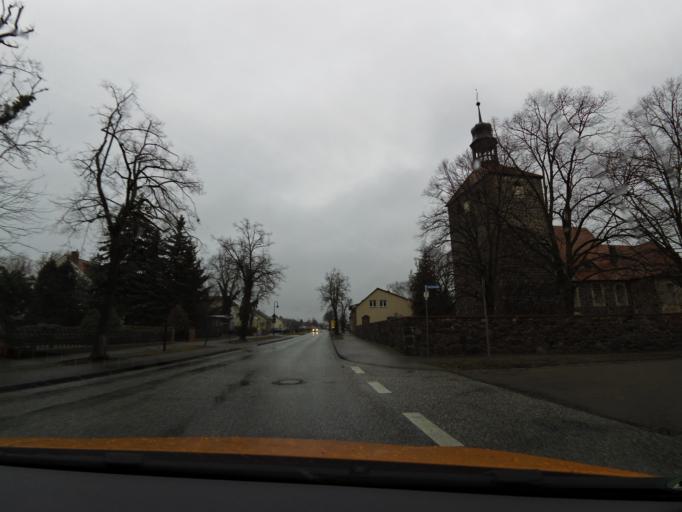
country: DE
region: Brandenburg
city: Rangsdorf
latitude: 52.2746
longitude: 13.4646
